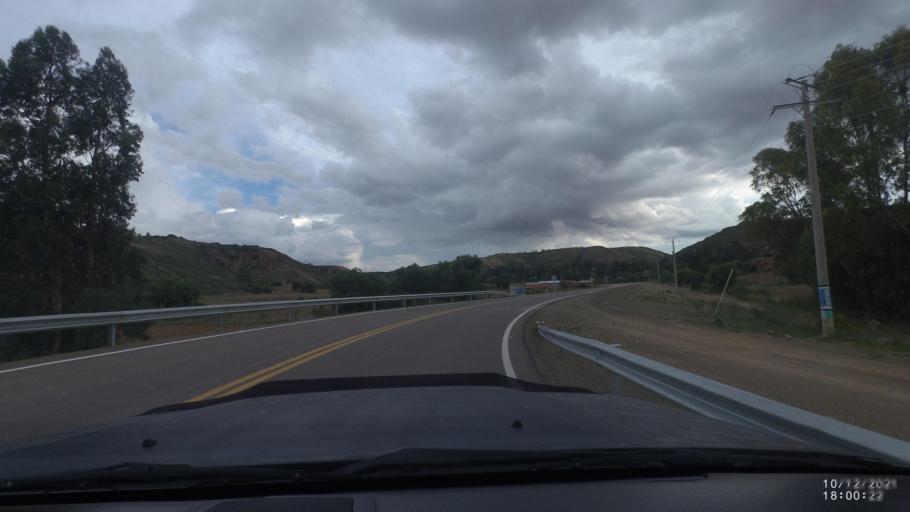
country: BO
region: Cochabamba
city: Cliza
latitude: -17.7412
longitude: -65.9218
